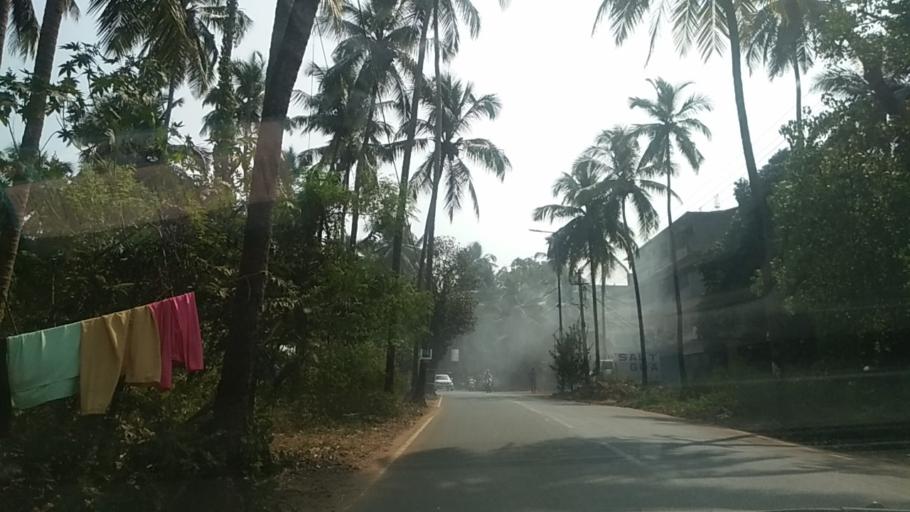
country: IN
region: Goa
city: Calangute
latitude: 15.5533
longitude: 73.7638
